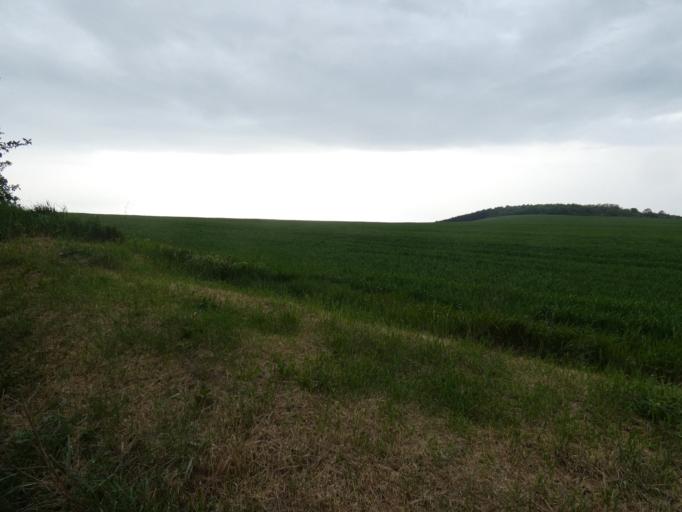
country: HU
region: Pest
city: Pilisborosjeno
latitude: 47.6034
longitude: 18.9882
